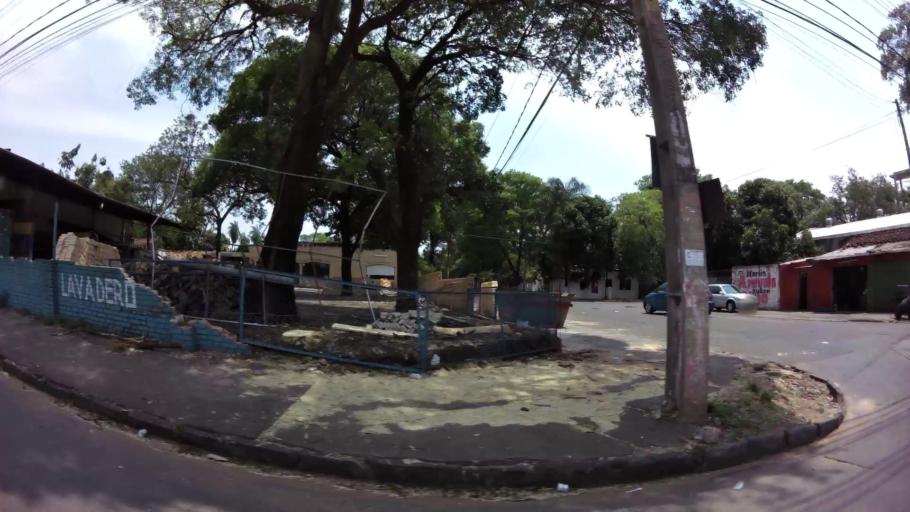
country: PY
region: Central
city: Lambare
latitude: -25.3139
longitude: -57.5720
